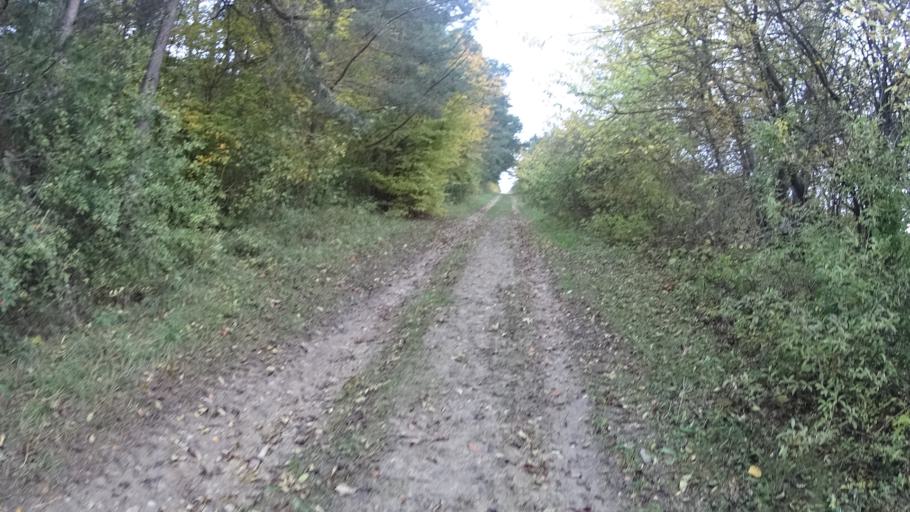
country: DE
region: Thuringia
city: Arnstadt
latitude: 50.8381
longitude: 10.9040
